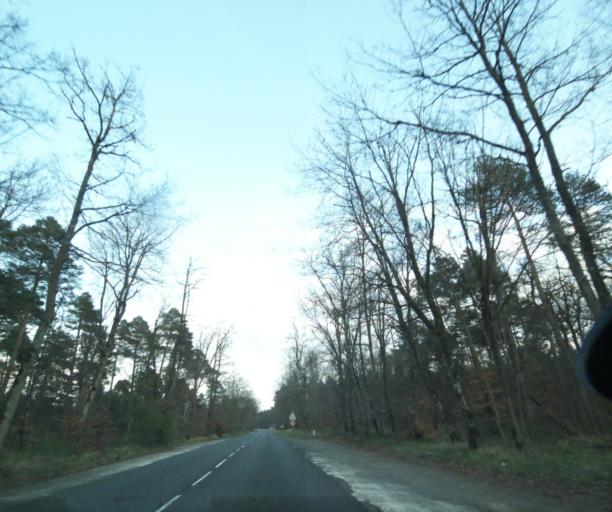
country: FR
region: Ile-de-France
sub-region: Departement de Seine-et-Marne
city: Avon
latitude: 48.3781
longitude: 2.7362
